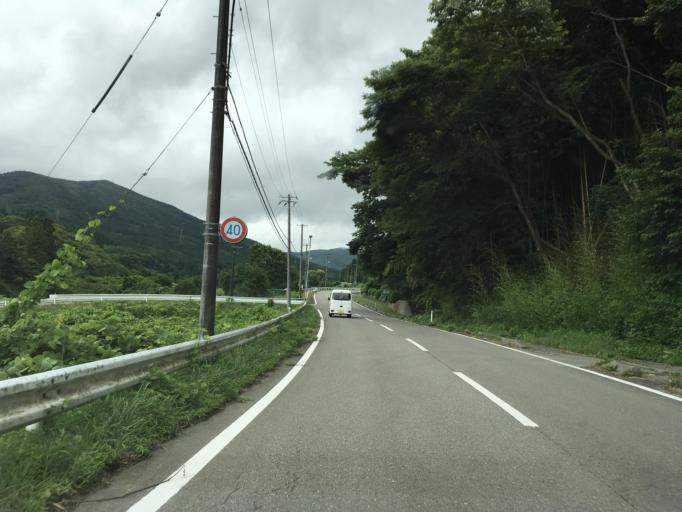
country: JP
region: Iwate
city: Ofunato
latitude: 38.8953
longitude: 141.4860
